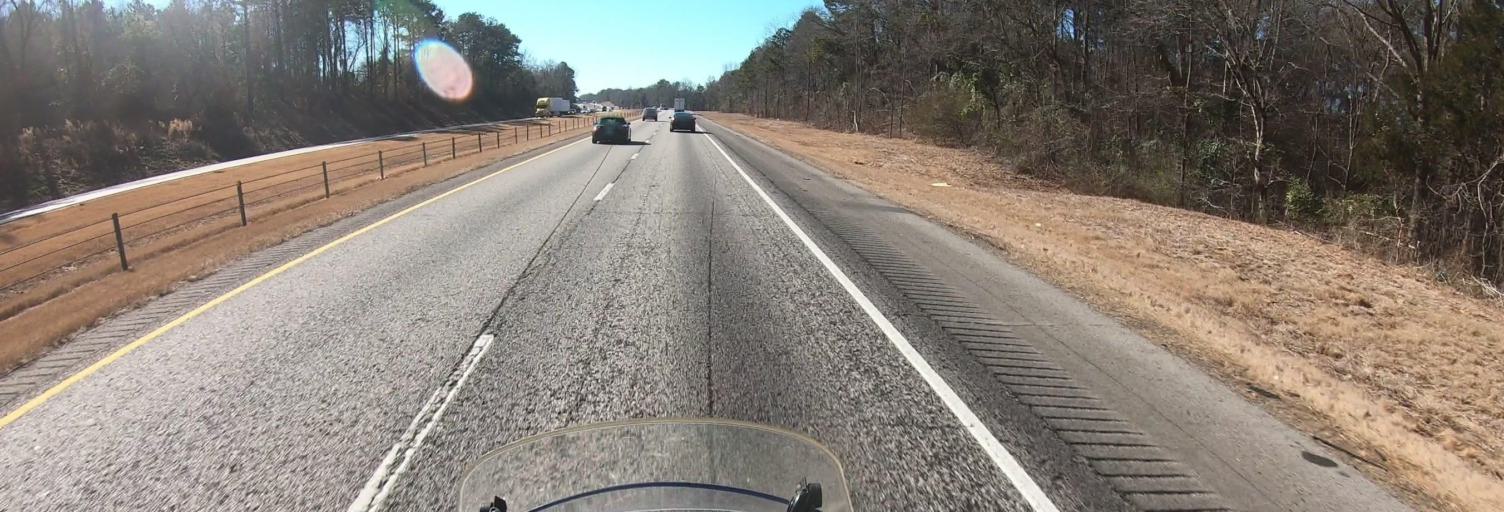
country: US
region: Georgia
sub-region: Banks County
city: Maysville
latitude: 34.2117
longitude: -83.5374
